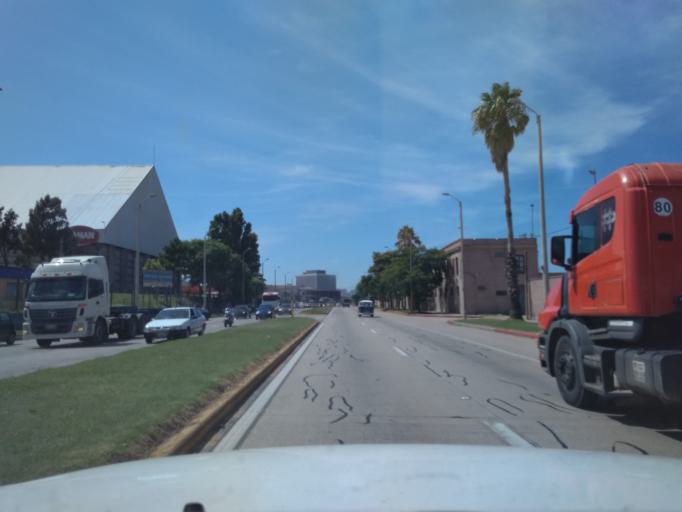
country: UY
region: Montevideo
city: Montevideo
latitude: -34.8796
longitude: -56.2037
